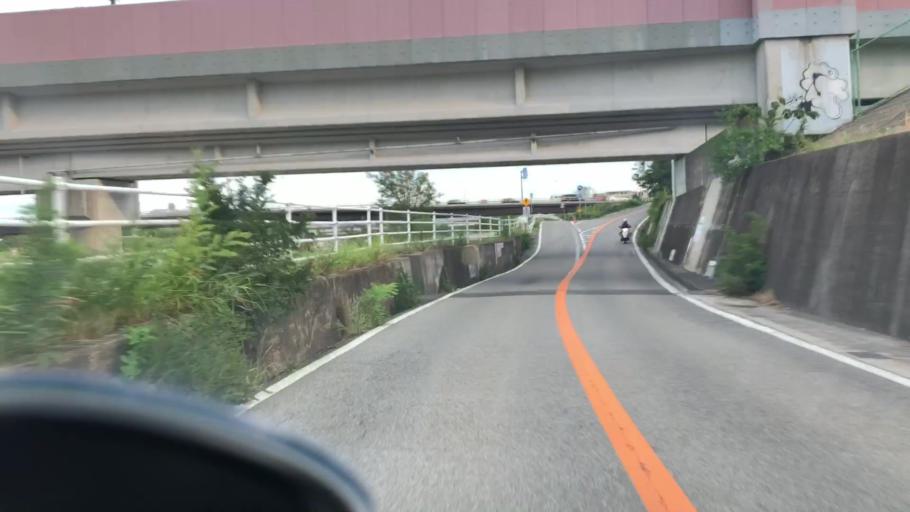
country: JP
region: Hyogo
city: Itami
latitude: 34.7490
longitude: 135.3747
